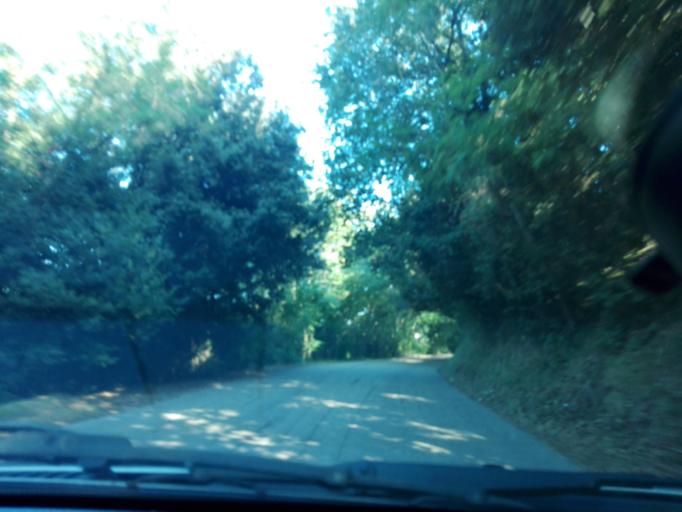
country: IT
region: Abruzzo
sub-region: Provincia di Pescara
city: Cappelle sul Tavo
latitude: 42.4481
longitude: 14.0908
